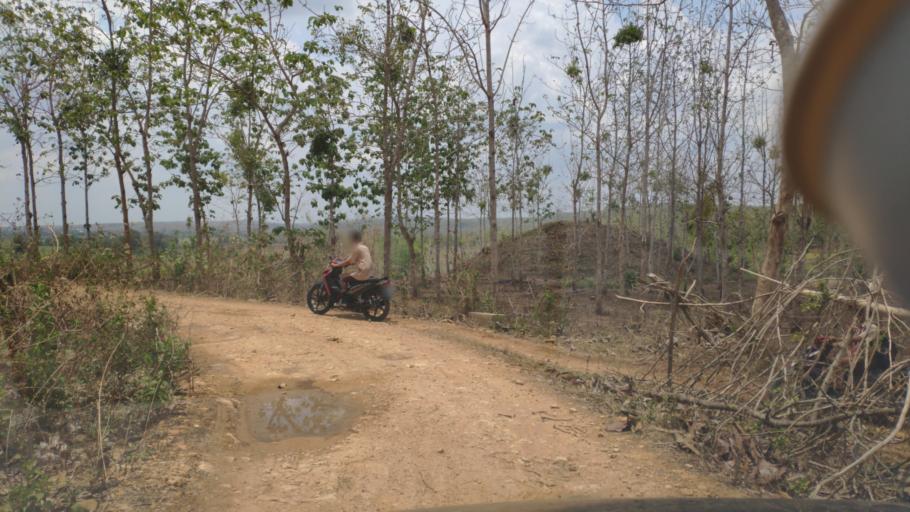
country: ID
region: Central Java
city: Ngapus
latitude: -6.9615
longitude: 111.2238
